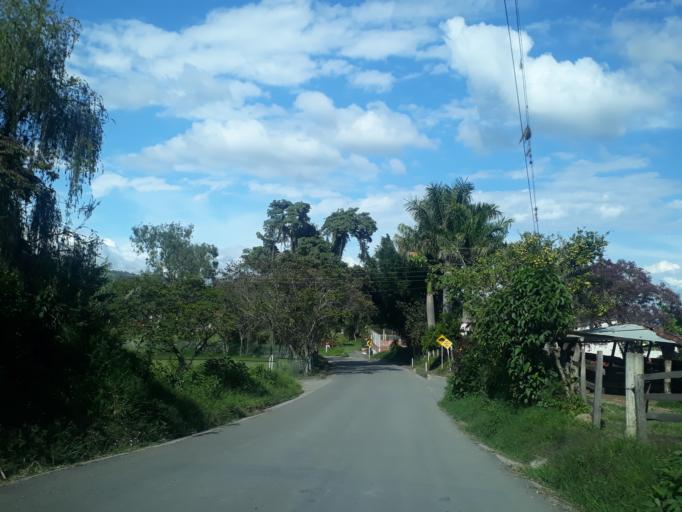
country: CO
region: Santander
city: Velez
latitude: 6.0435
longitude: -73.6516
